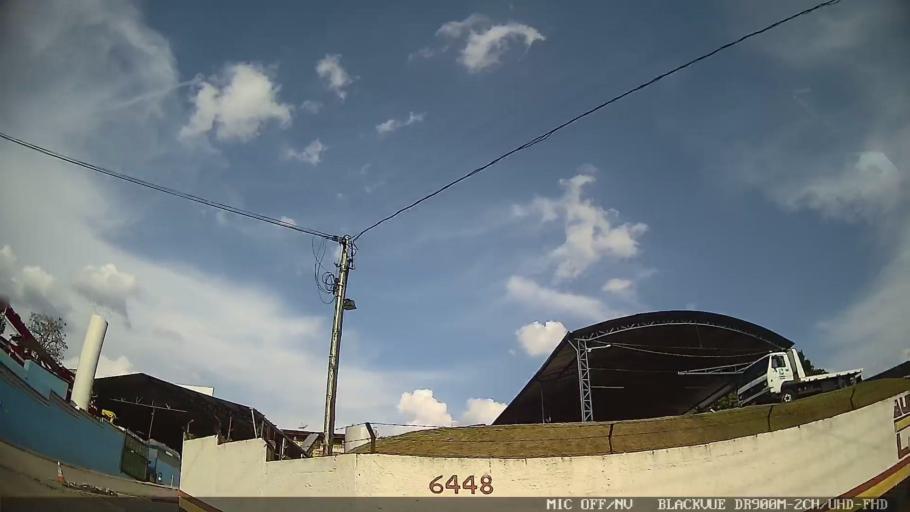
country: BR
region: Sao Paulo
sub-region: Braganca Paulista
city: Braganca Paulista
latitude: -22.9230
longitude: -46.5502
